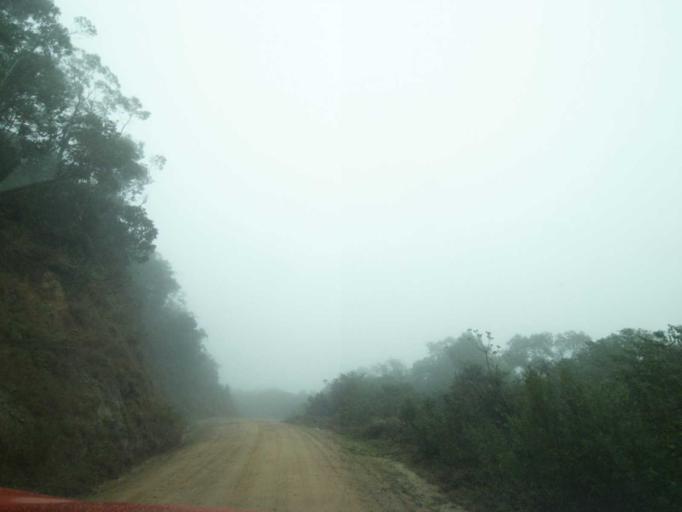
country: BR
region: Santa Catarina
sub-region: Anitapolis
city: Anitapolis
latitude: -27.9226
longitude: -49.1793
